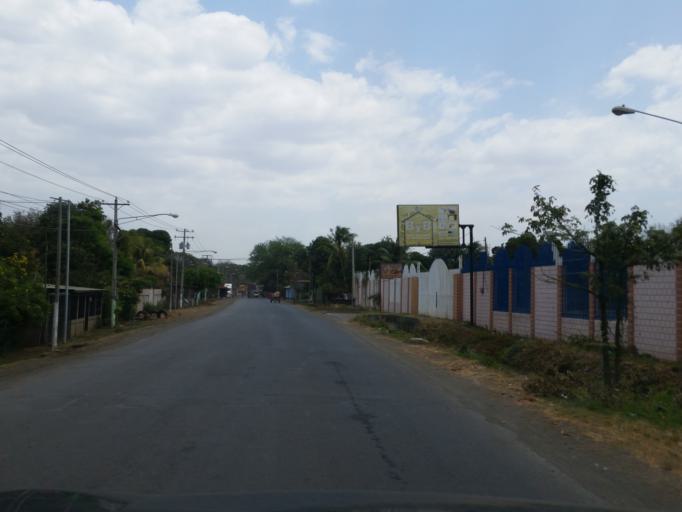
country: NI
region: Managua
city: Managua
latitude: 12.1249
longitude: -86.1761
